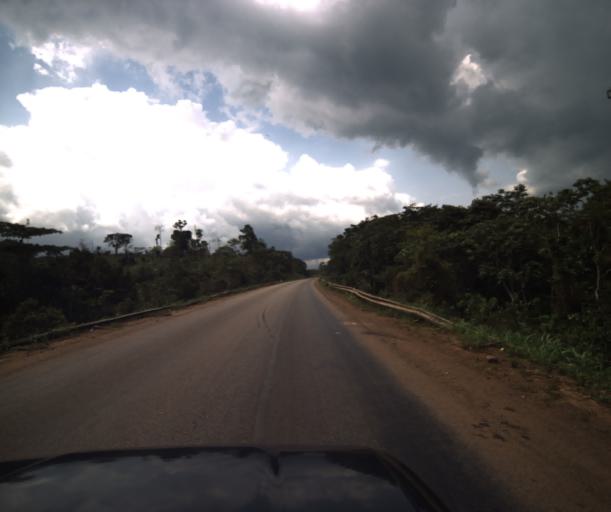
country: CM
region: Littoral
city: Edea
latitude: 3.9313
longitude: 10.0551
